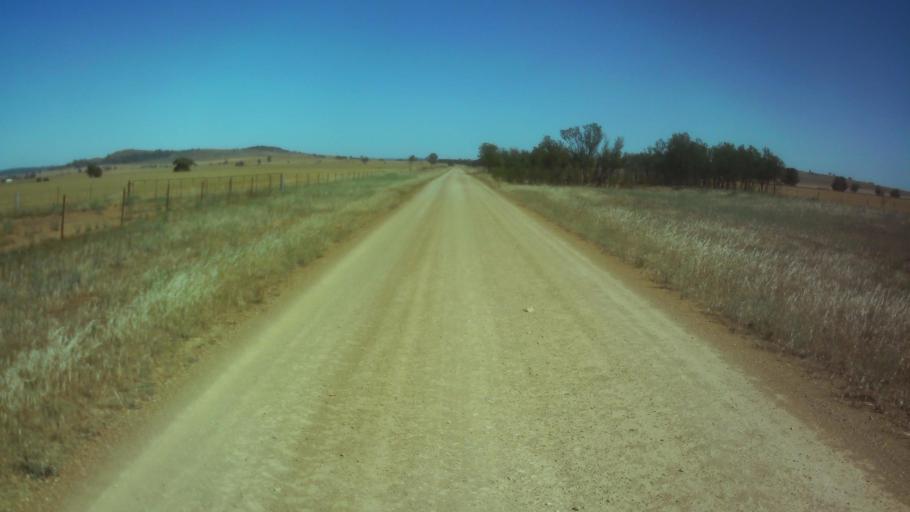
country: AU
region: New South Wales
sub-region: Weddin
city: Grenfell
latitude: -33.9814
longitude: 148.3290
